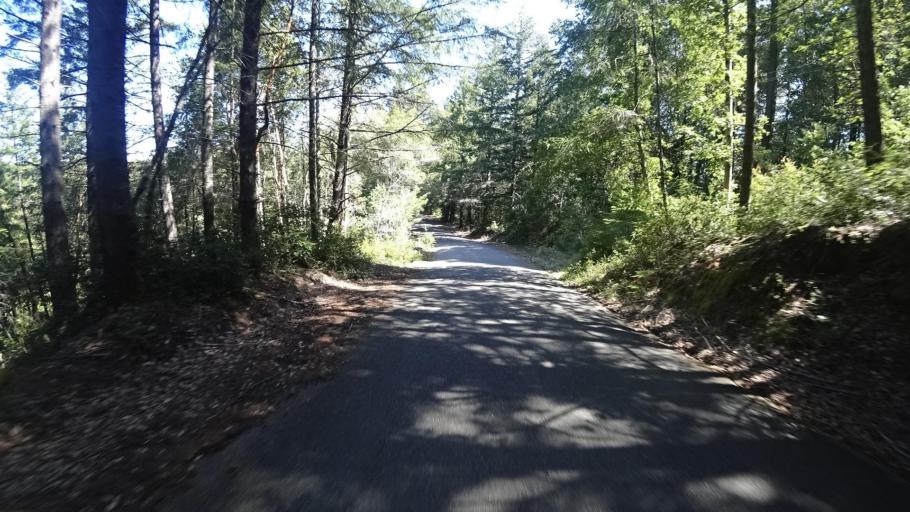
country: US
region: California
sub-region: Humboldt County
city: Redway
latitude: 40.1897
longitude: -124.0942
